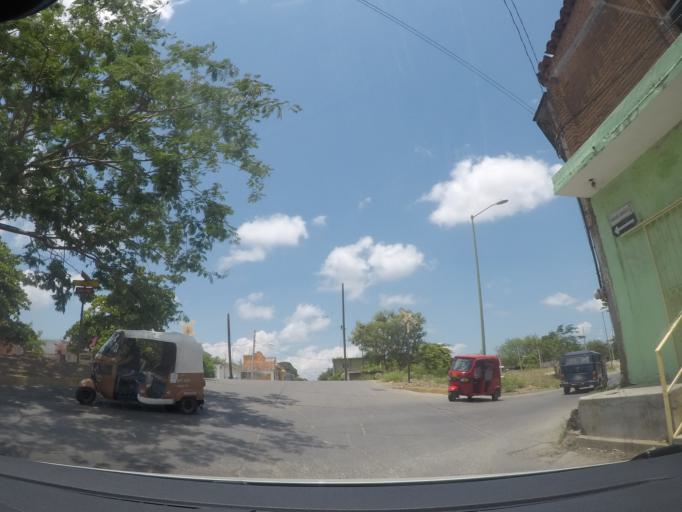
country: MX
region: Oaxaca
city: Juchitan de Zaragoza
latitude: 16.4409
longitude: -95.0187
